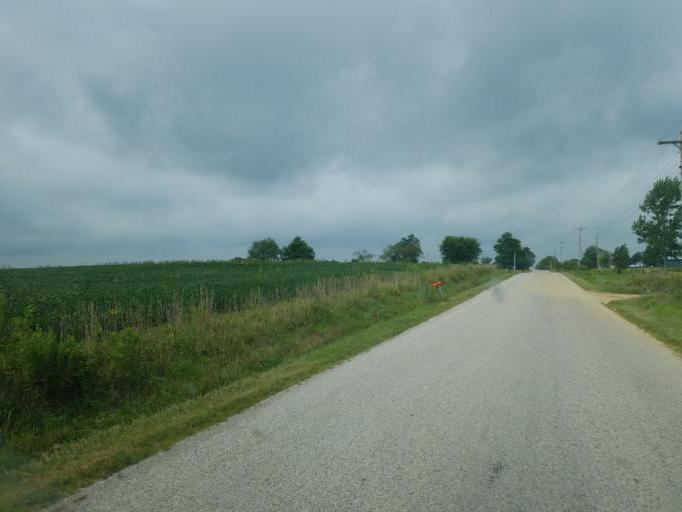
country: US
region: Ohio
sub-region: Morrow County
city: Mount Gilead
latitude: 40.4807
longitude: -82.8055
